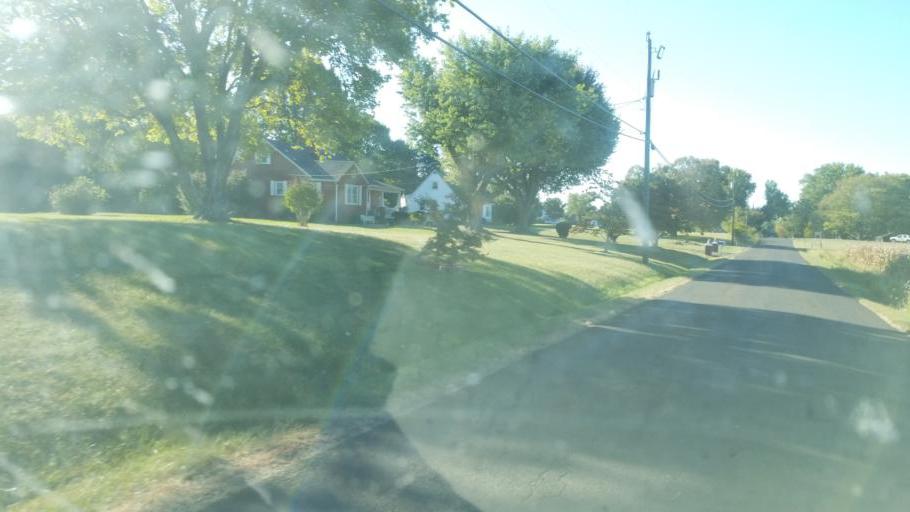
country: US
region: Virginia
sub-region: Fauquier County
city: Bealeton
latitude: 38.5987
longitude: -77.7711
